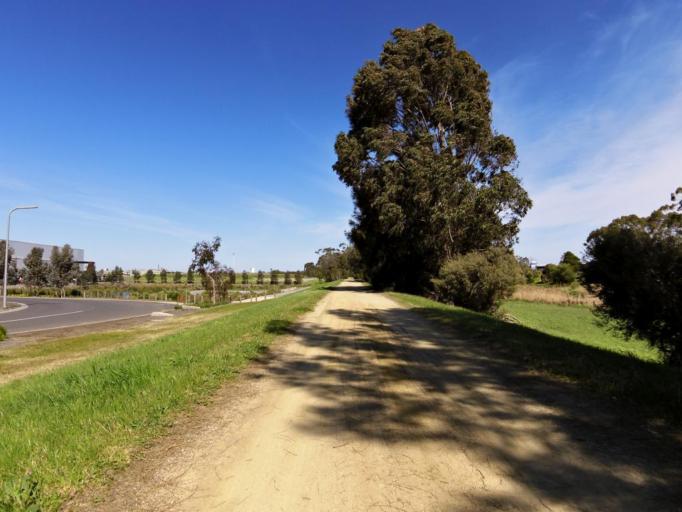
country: AU
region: Victoria
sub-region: Greater Dandenong
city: Keysborough
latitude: -38.0172
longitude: 145.1893
